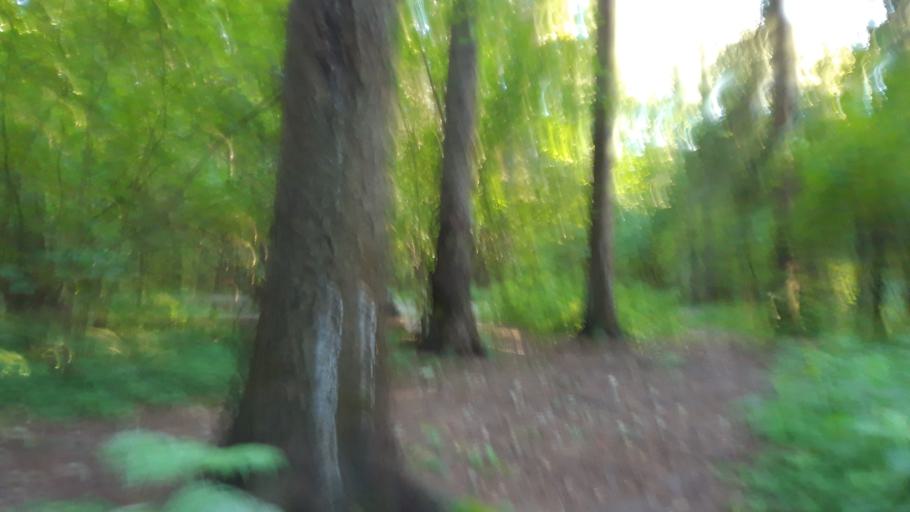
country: RU
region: Moscow
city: Zelenograd
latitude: 55.9851
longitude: 37.1970
